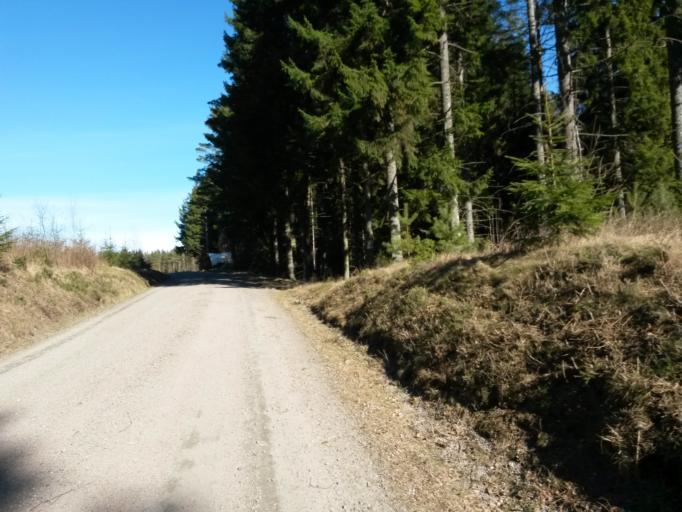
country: SE
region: Vaestra Goetaland
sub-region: Vargarda Kommun
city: Jonstorp
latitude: 57.9798
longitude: 12.7515
